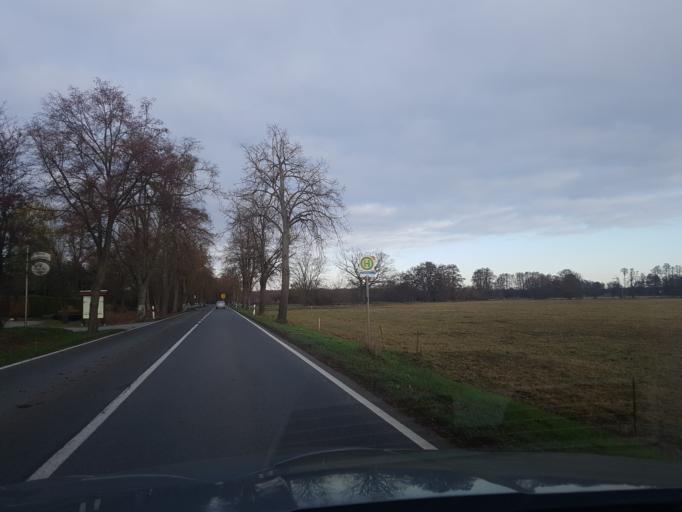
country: DE
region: Brandenburg
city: Golssen
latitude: 51.9660
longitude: 13.6156
